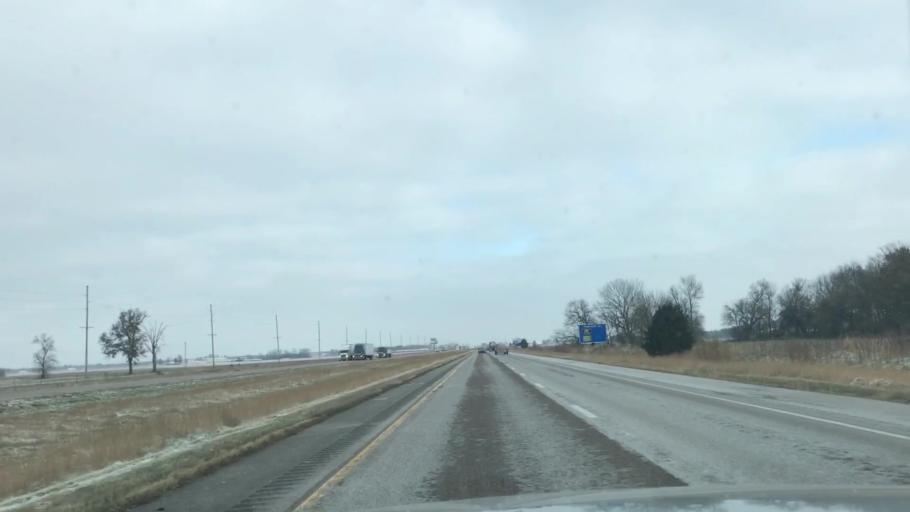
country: US
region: Illinois
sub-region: Macoupin County
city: Staunton
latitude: 38.9921
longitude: -89.7495
